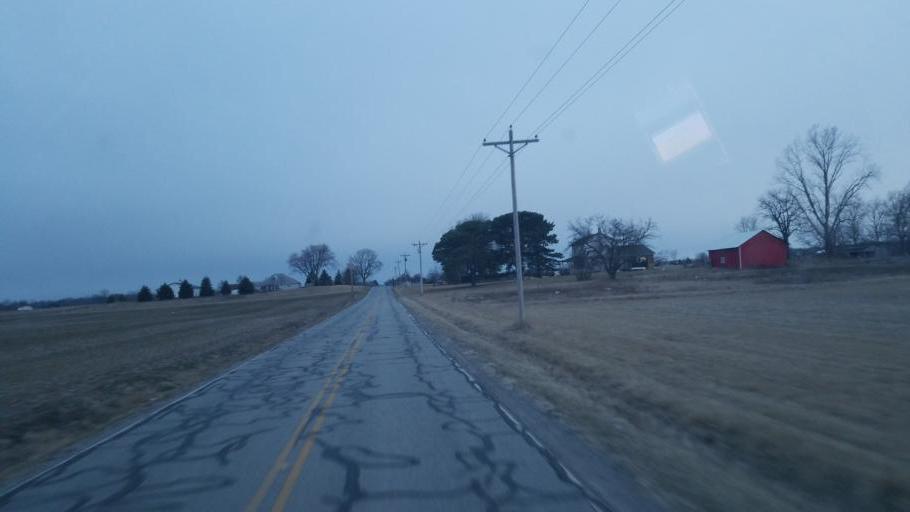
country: US
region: Ohio
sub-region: Defiance County
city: Hicksville
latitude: 41.3250
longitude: -84.7390
